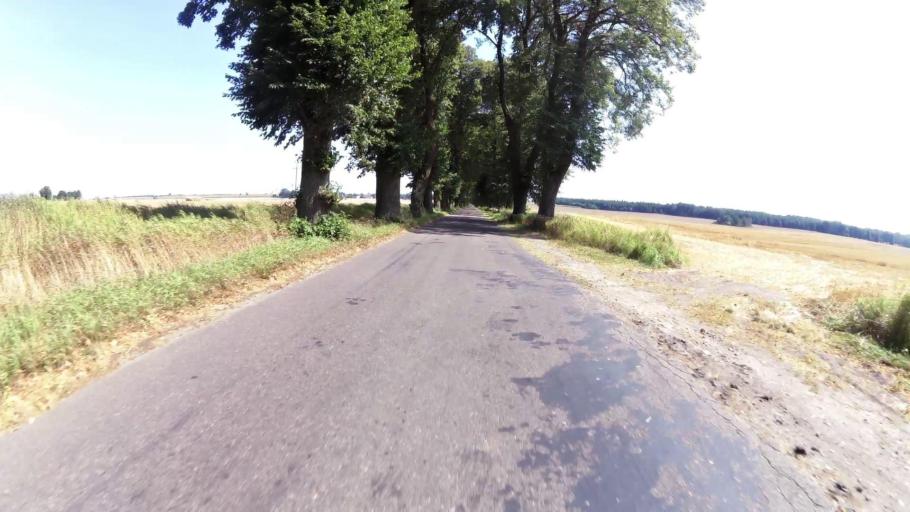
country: PL
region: West Pomeranian Voivodeship
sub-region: Powiat walecki
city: Walcz
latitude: 53.2000
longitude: 16.5146
